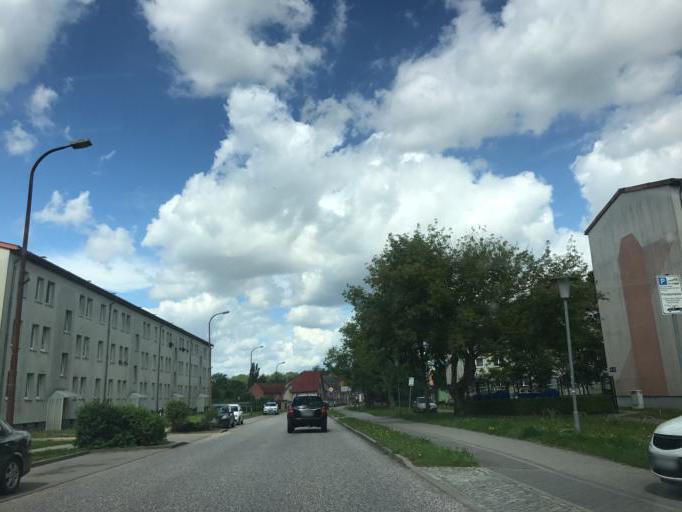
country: DE
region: Brandenburg
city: Gransee
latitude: 53.0040
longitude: 13.1522
